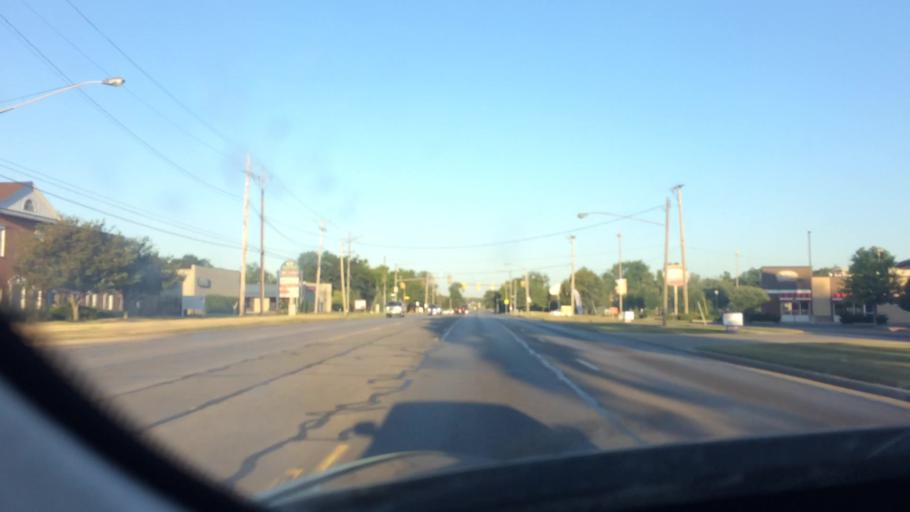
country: US
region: Ohio
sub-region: Lucas County
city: Holland
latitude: 41.6158
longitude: -83.6742
